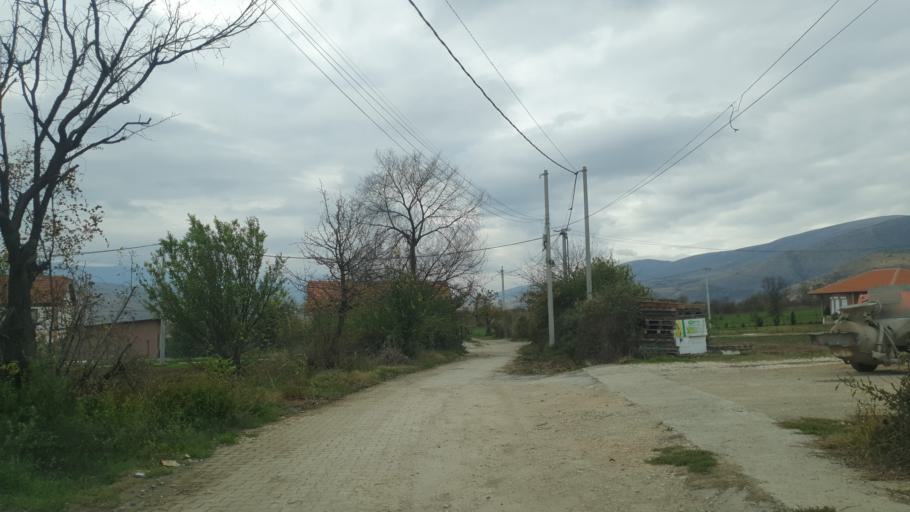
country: MK
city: Kondovo
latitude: 42.0423
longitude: 21.2772
